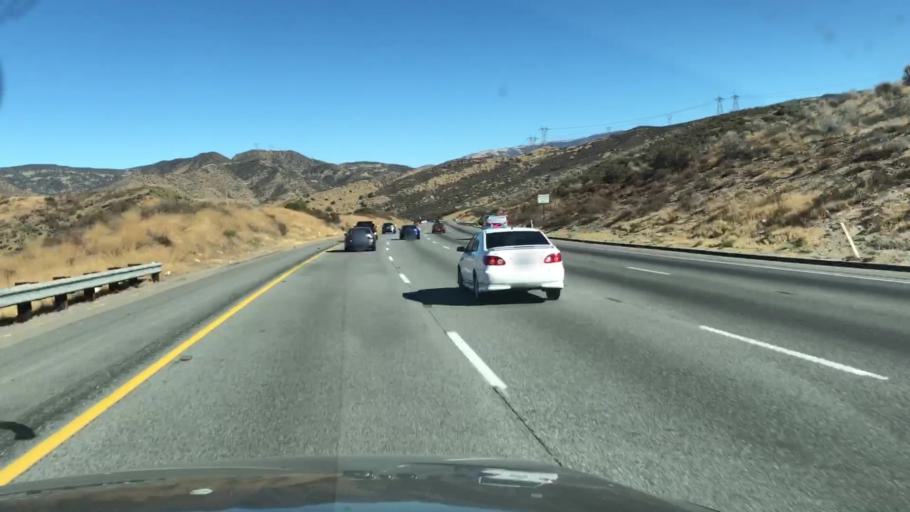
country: US
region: California
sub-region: Los Angeles County
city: Castaic
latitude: 34.6060
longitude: -118.7116
